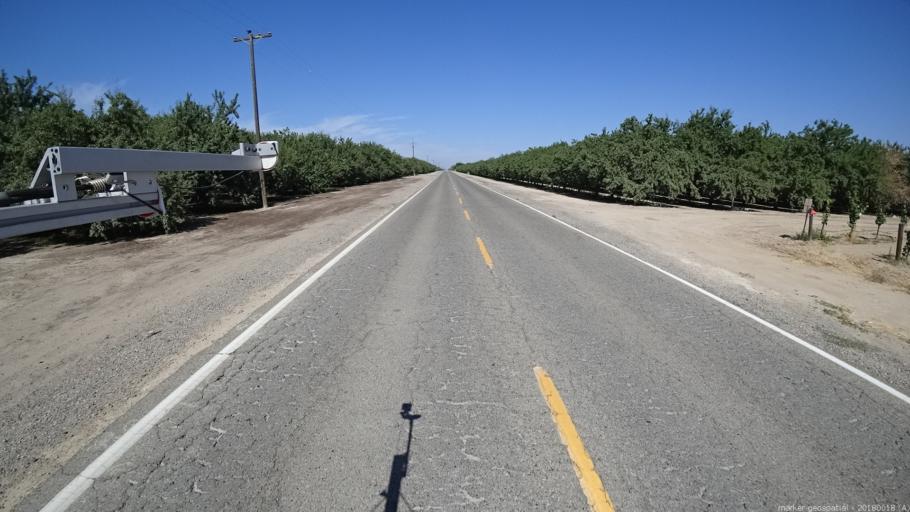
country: US
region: California
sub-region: Madera County
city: Parkwood
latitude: 36.8511
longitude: -120.1874
